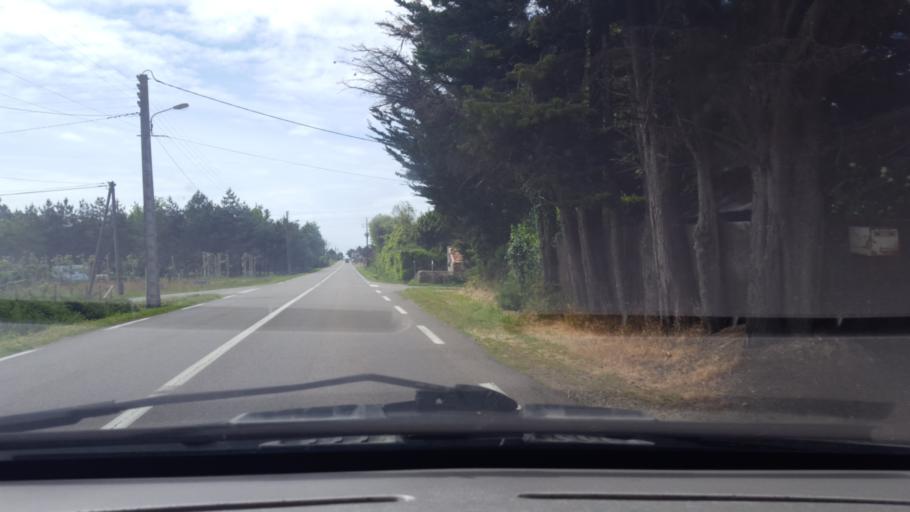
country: FR
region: Pays de la Loire
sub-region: Departement de la Loire-Atlantique
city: Bourgneuf-en-Retz
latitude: 47.0287
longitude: -1.8967
